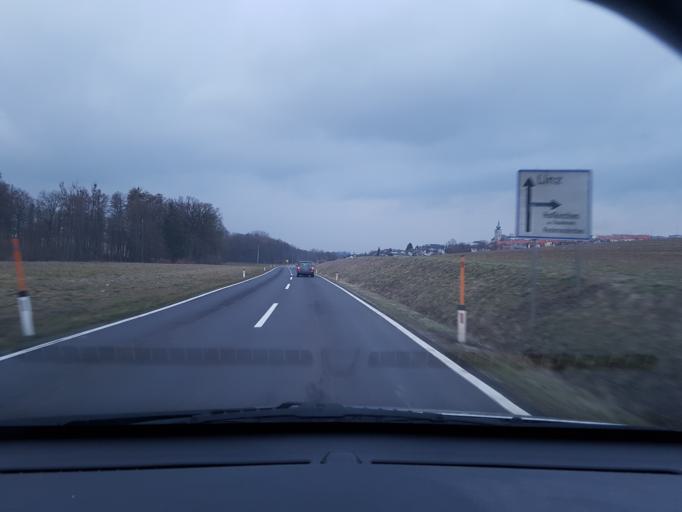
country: AT
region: Upper Austria
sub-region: Politischer Bezirk Linz-Land
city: Sankt Florian
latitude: 48.1550
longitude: 14.3323
